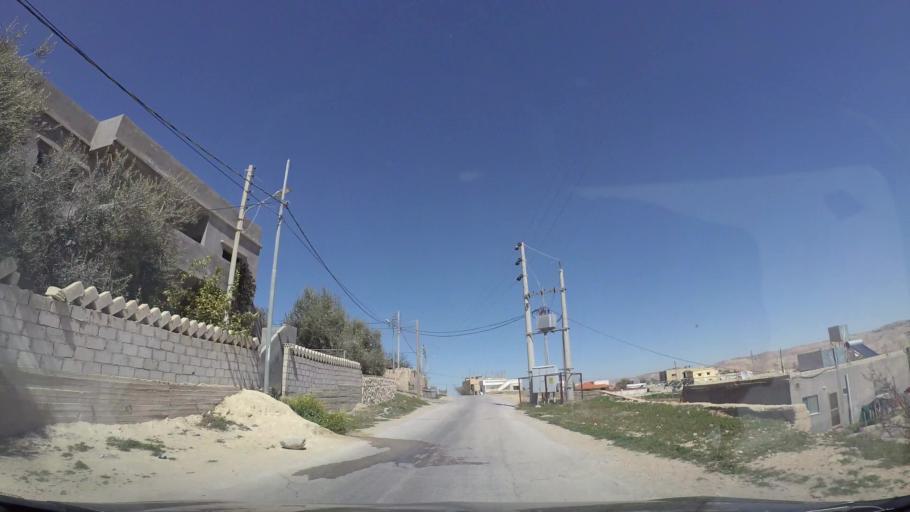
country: JO
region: Tafielah
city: At Tafilah
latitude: 30.8272
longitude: 35.5798
